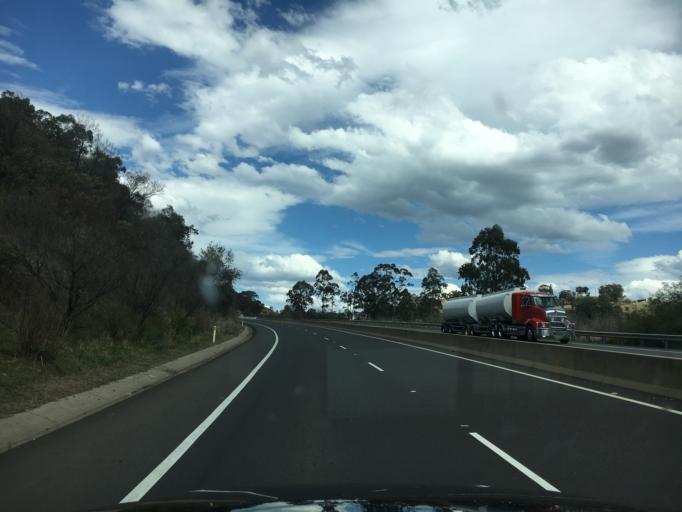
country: AU
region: New South Wales
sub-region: Liverpool Plains
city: Quirindi
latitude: -31.7367
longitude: 150.7876
